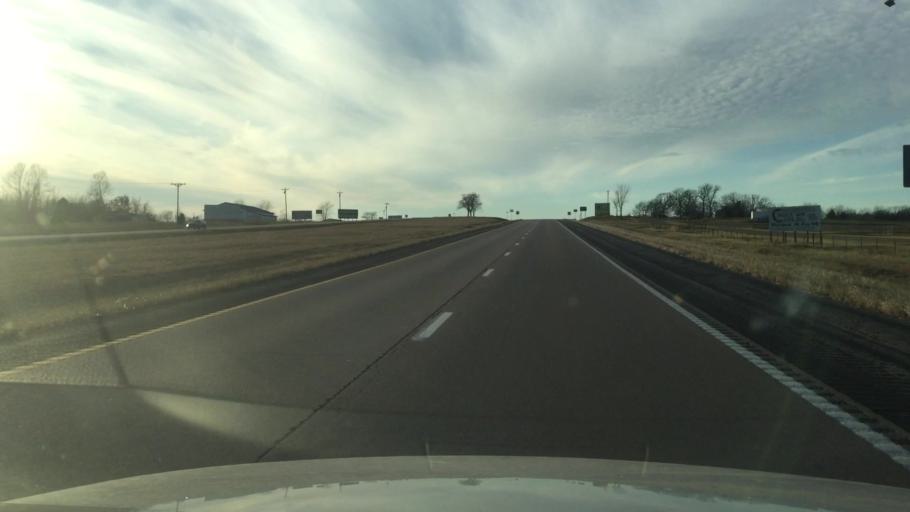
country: US
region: Missouri
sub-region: Miller County
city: Eldon
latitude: 38.3679
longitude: -92.5005
